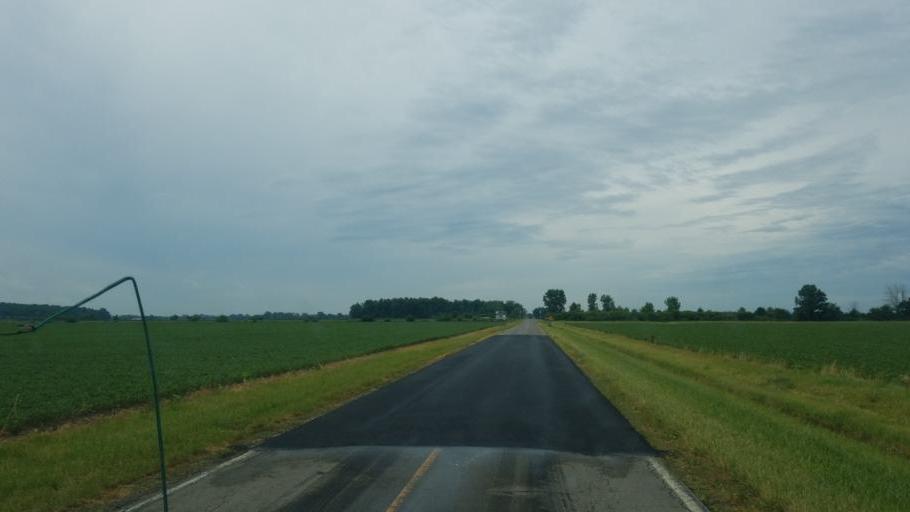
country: US
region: Ohio
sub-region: Defiance County
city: Hicksville
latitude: 41.2954
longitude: -84.6896
